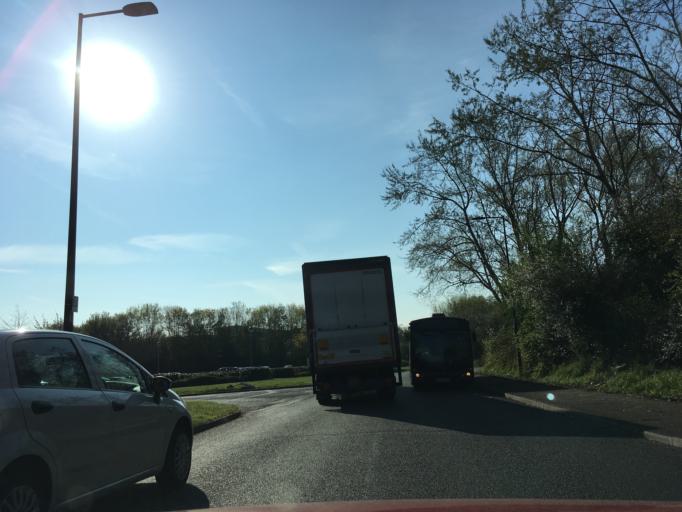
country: GB
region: England
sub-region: Milton Keynes
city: Newport Pagnell
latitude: 52.0682
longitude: -0.7301
